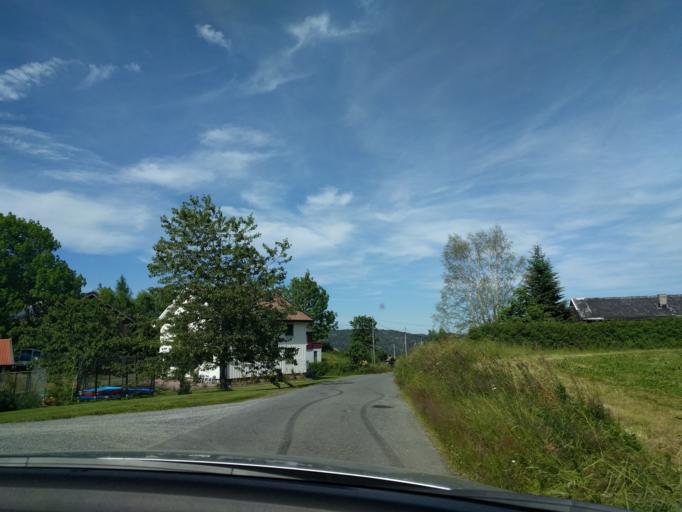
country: NO
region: Aust-Agder
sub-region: Gjerstad
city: Gjerstad
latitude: 58.8856
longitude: 8.9511
